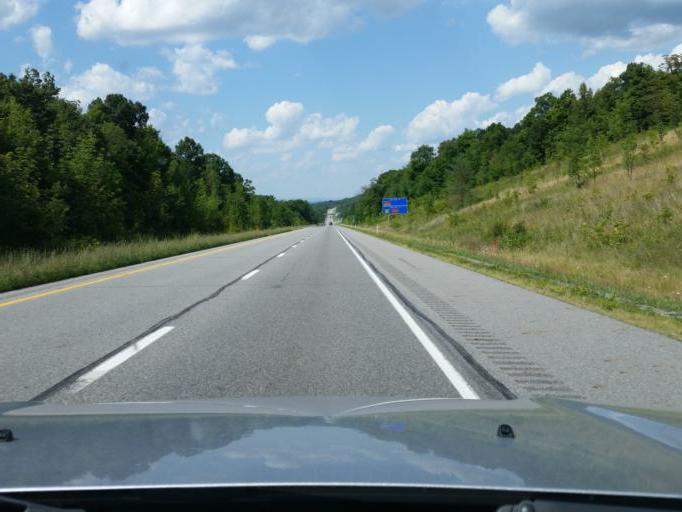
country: US
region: Pennsylvania
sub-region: Blair County
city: Claysburg
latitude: 40.2441
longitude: -78.4602
